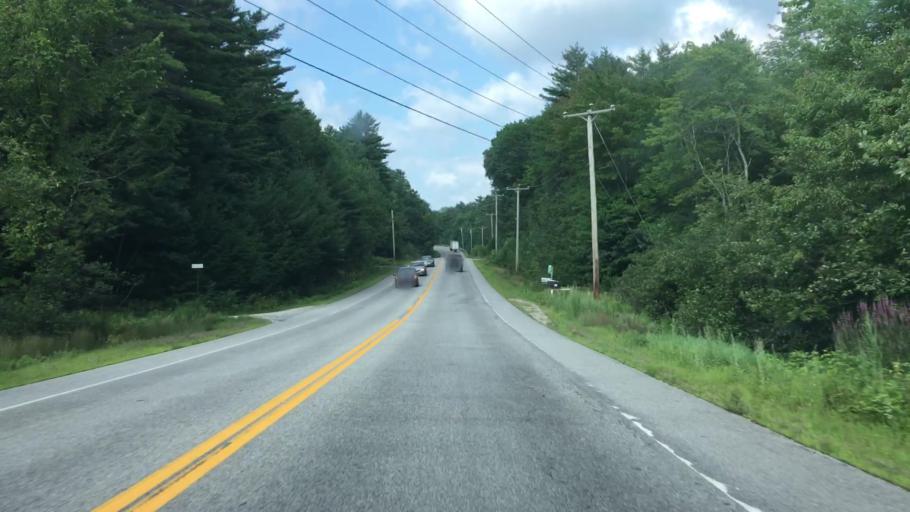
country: US
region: Maine
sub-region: Androscoggin County
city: Minot
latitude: 44.0285
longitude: -70.3055
